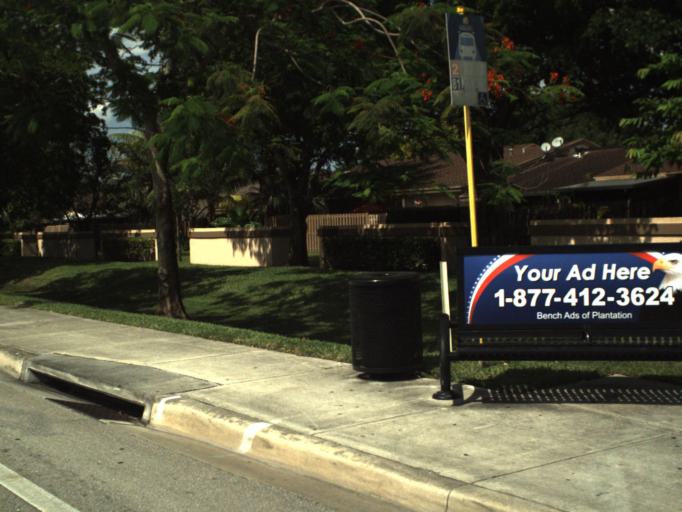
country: US
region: Florida
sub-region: Broward County
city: Plantation
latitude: 26.1344
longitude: -80.2566
